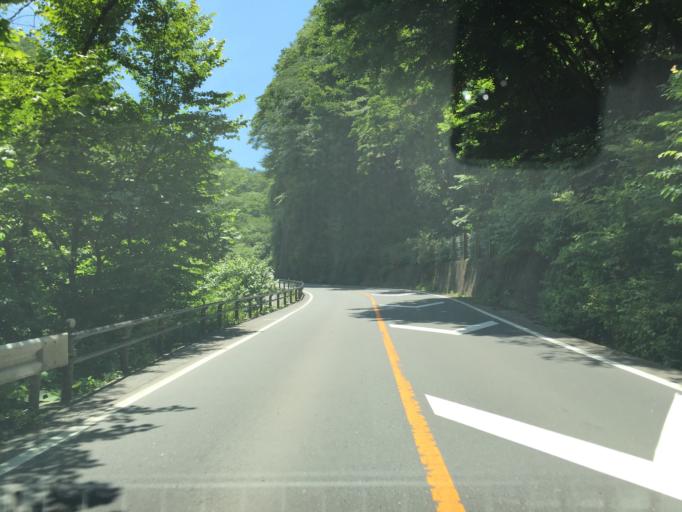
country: JP
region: Miyagi
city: Marumori
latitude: 37.7701
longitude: 140.7975
